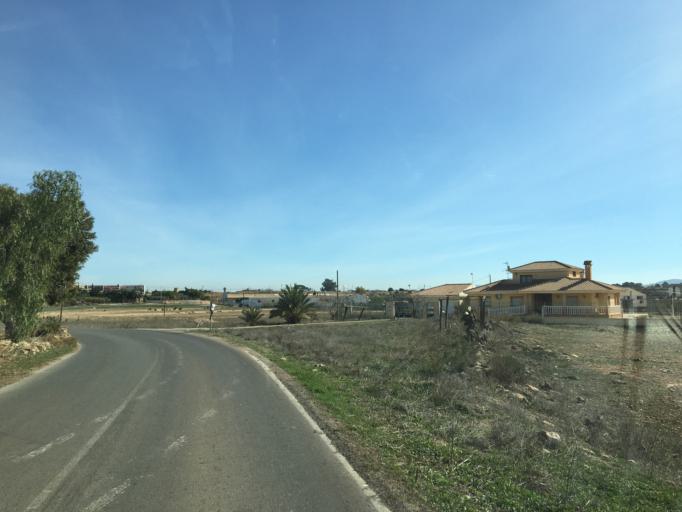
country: ES
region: Murcia
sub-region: Murcia
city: Cartagena
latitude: 37.6327
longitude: -1.0242
